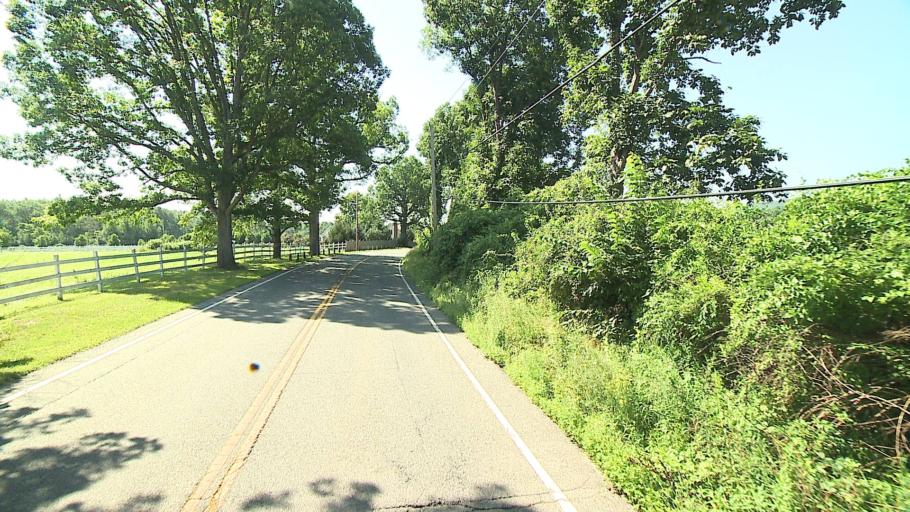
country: US
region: Connecticut
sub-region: Litchfield County
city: Canaan
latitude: 42.0423
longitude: -73.4236
